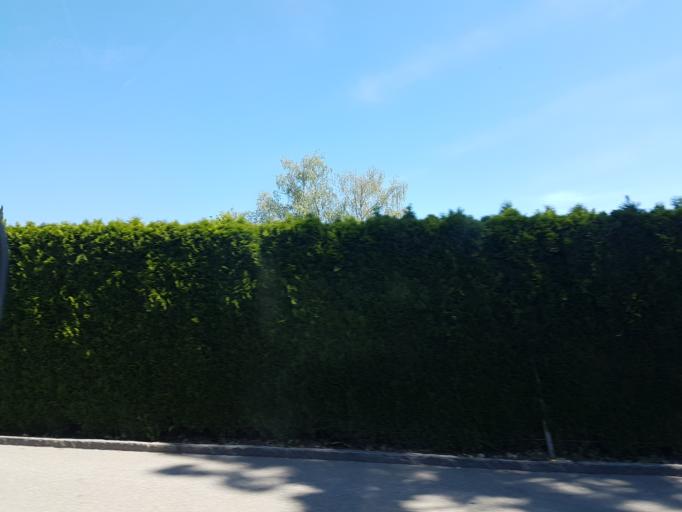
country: CH
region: Zurich
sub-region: Bezirk Affoltern
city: Affoltern / Unterdorf
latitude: 47.2832
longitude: 8.4459
